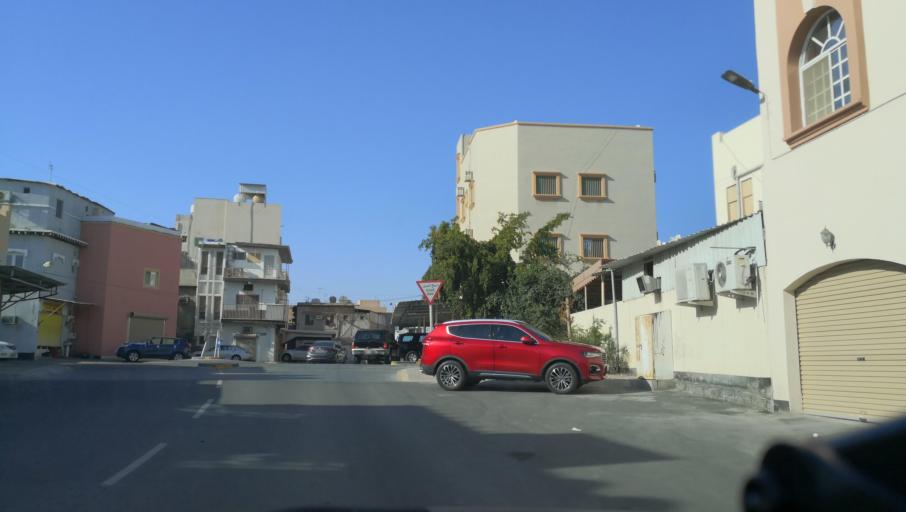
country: BH
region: Muharraq
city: Al Muharraq
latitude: 26.2512
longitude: 50.6329
